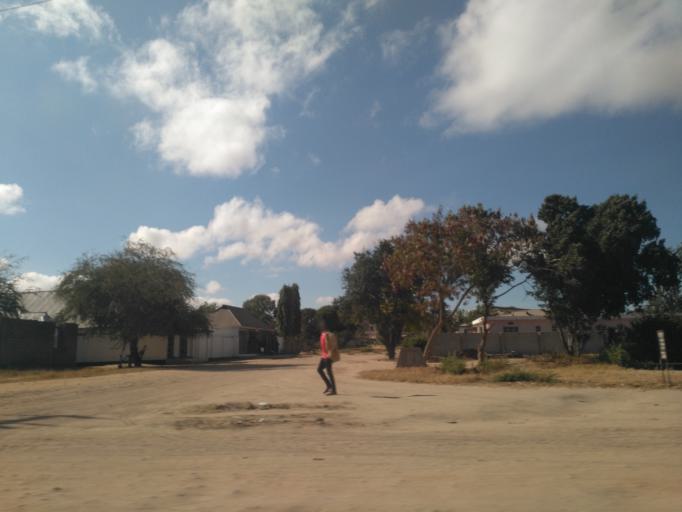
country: TZ
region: Dodoma
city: Dodoma
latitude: -6.1867
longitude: 35.7361
